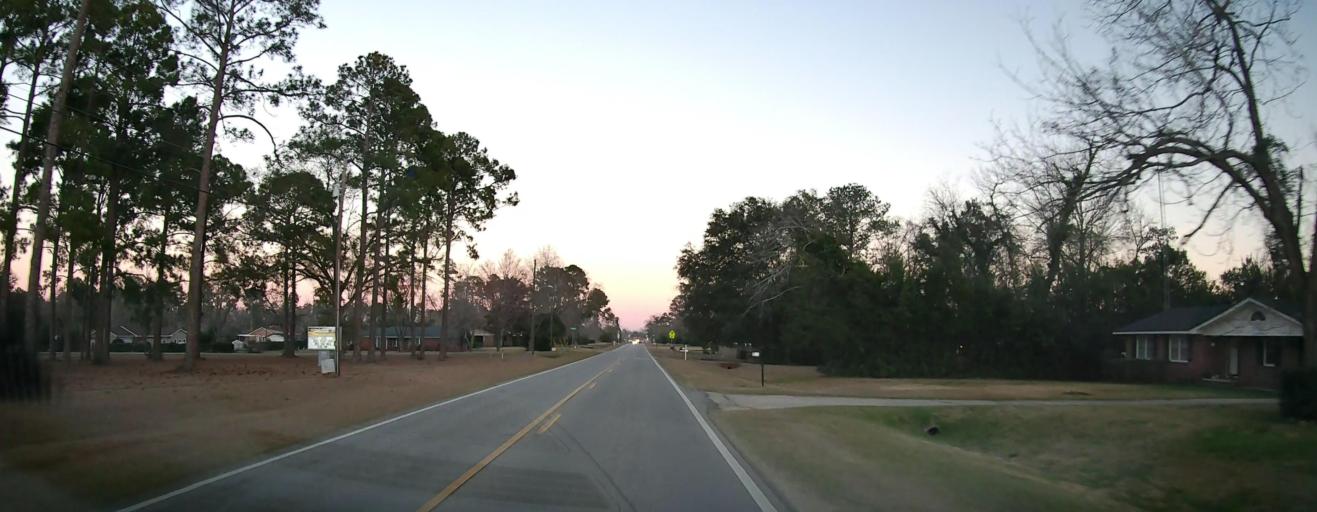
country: US
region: Georgia
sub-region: Dougherty County
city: Albany
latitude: 31.5293
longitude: -84.1284
